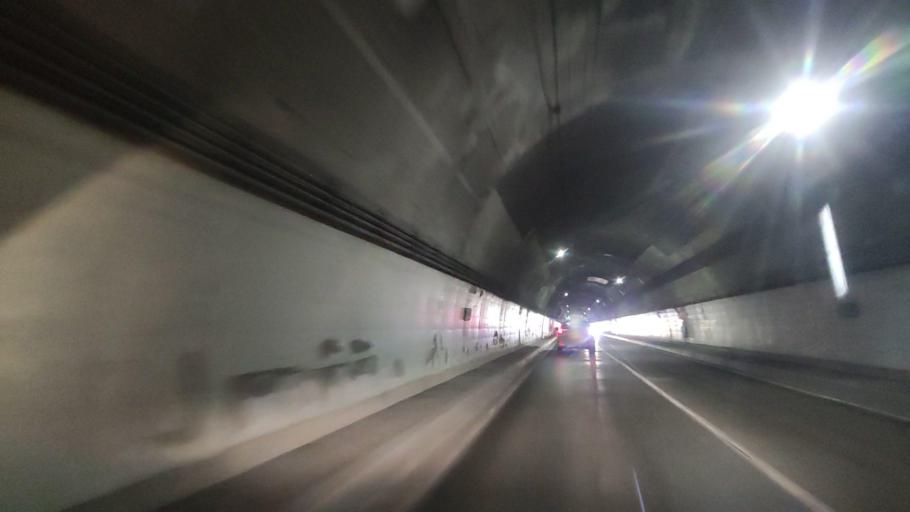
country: JP
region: Hokkaido
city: Ishikari
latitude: 43.4421
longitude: 141.4141
